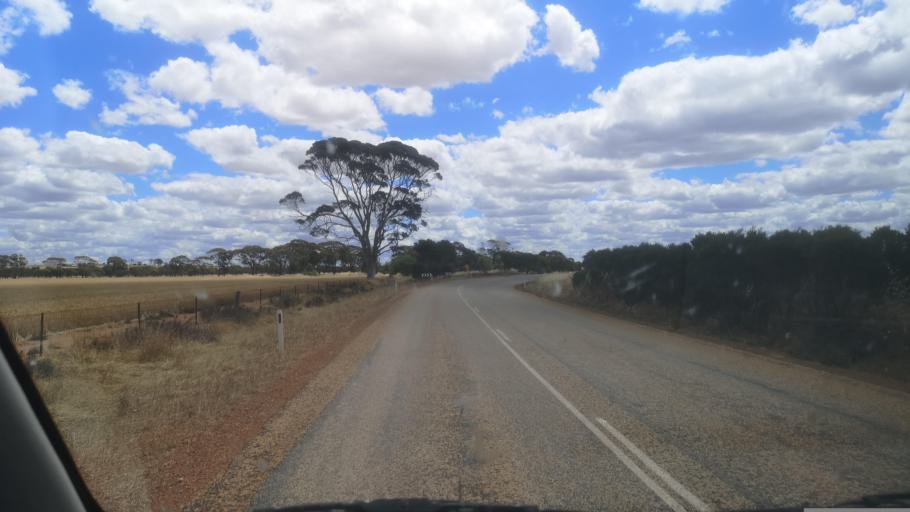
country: AU
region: Western Australia
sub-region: Cunderdin
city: Cunderdin
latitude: -32.0801
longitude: 117.4445
